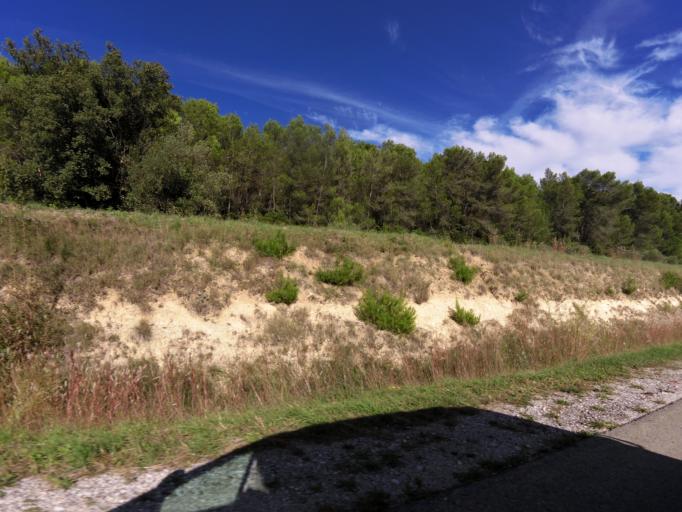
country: FR
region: Languedoc-Roussillon
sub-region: Departement du Gard
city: Aubais
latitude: 43.7769
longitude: 4.1427
